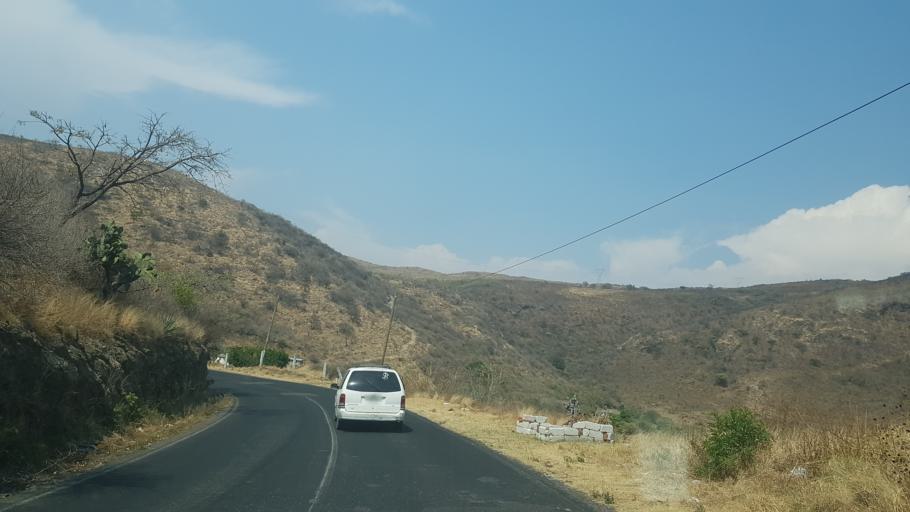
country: MX
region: Puebla
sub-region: Tianguismanalco
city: San Martin Tlapala
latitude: 18.9471
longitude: -98.4562
